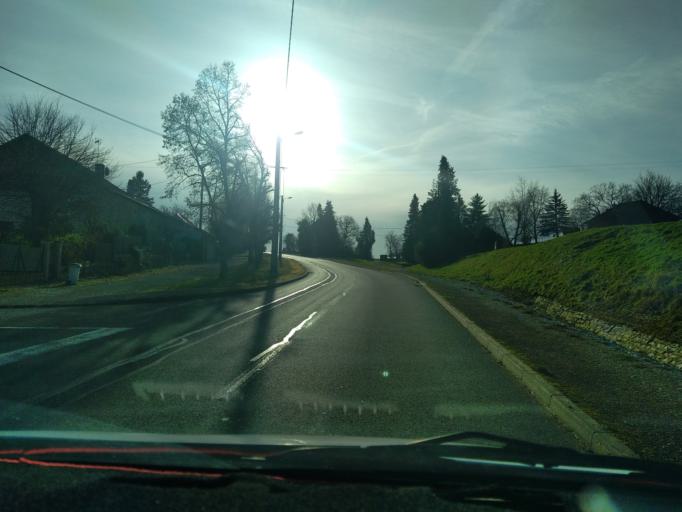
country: FR
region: Franche-Comte
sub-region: Departement de la Haute-Saone
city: Marnay
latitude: 47.3596
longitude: 5.6754
